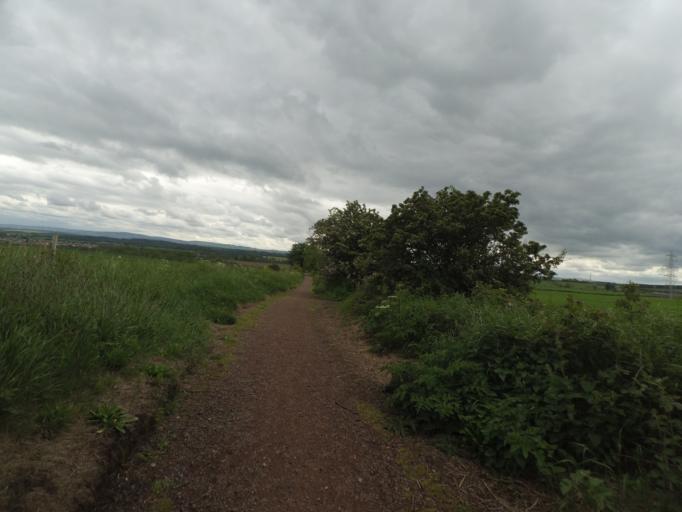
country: GB
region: Scotland
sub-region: East Lothian
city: Ormiston
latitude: 55.9177
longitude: -2.9673
